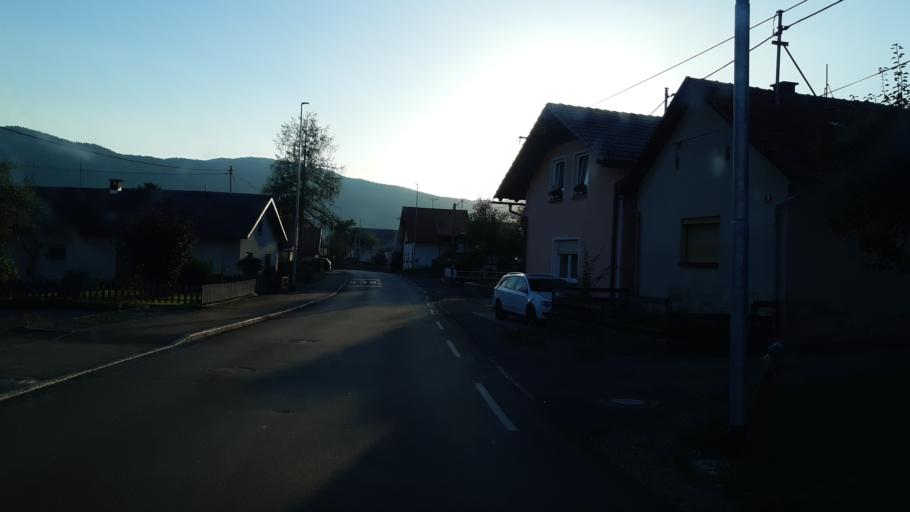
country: SI
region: Kocevje
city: Kocevje
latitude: 45.6452
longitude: 14.8781
